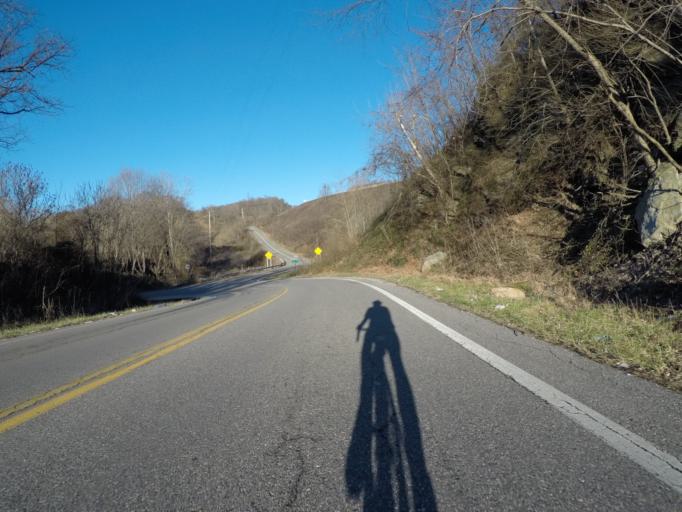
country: US
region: West Virginia
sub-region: Wayne County
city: Kenova
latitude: 38.3725
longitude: -82.5905
